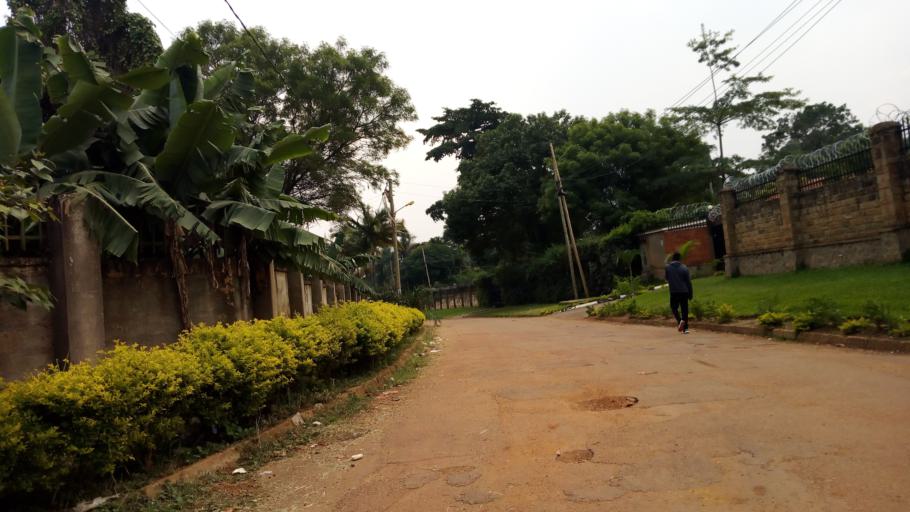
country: UG
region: Central Region
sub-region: Wakiso District
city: Kireka
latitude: 0.3214
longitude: 32.6292
